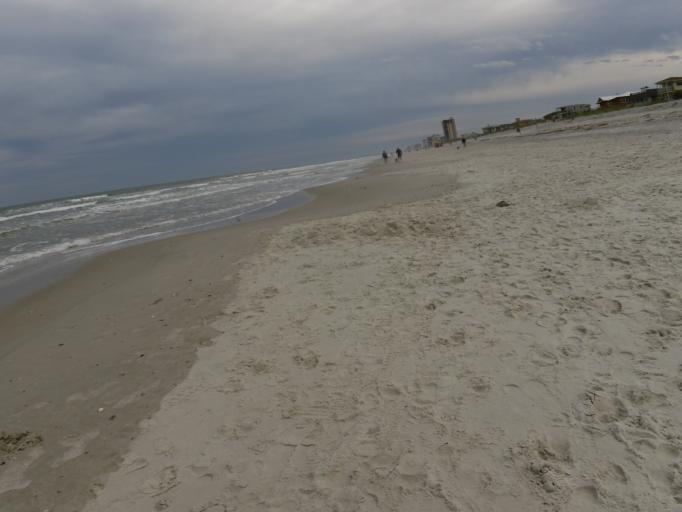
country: US
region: Florida
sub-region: Duval County
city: Neptune Beach
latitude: 30.3156
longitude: -81.3930
